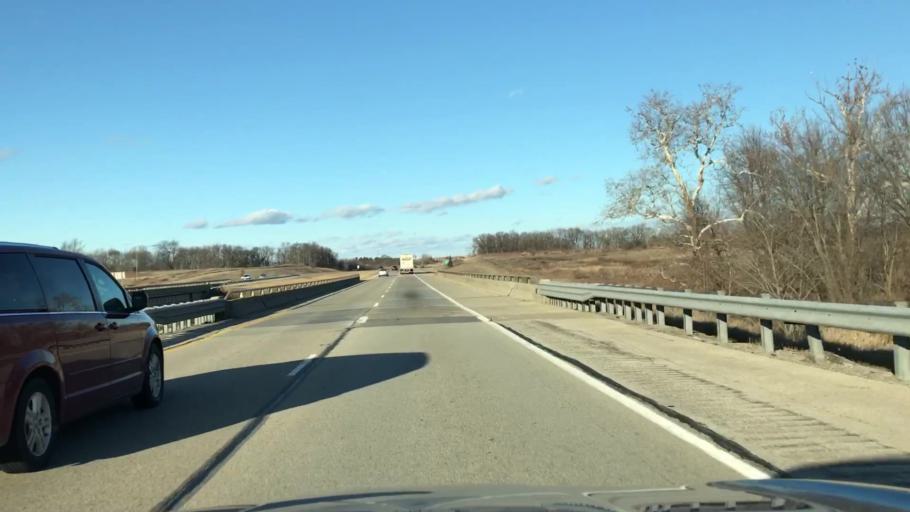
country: US
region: Illinois
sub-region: McLean County
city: Lexington
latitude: 40.6295
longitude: -88.8161
